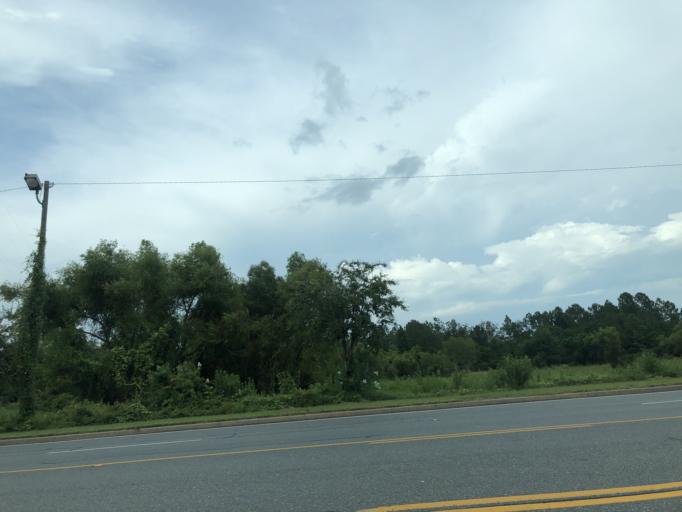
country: US
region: Georgia
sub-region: Wayne County
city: Jesup
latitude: 31.6197
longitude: -81.8999
